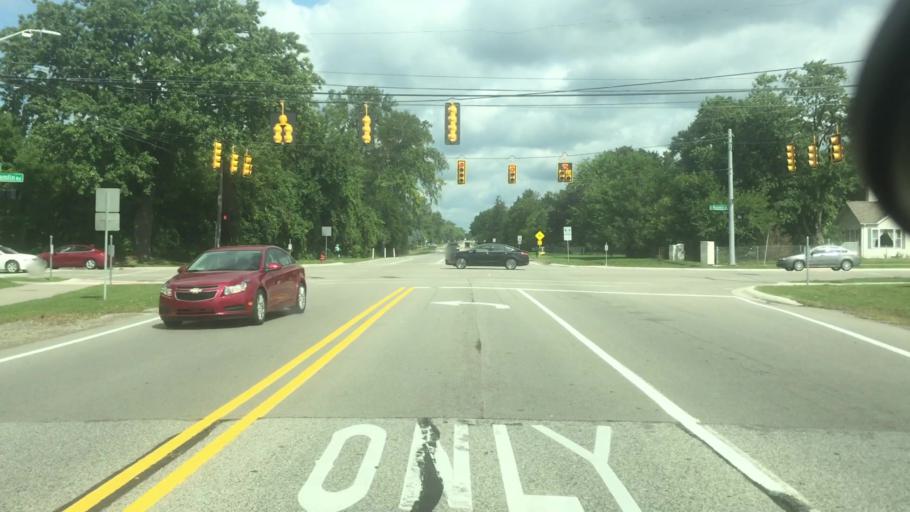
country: US
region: Michigan
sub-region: Oakland County
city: Rochester
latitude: 42.6526
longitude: -83.1125
